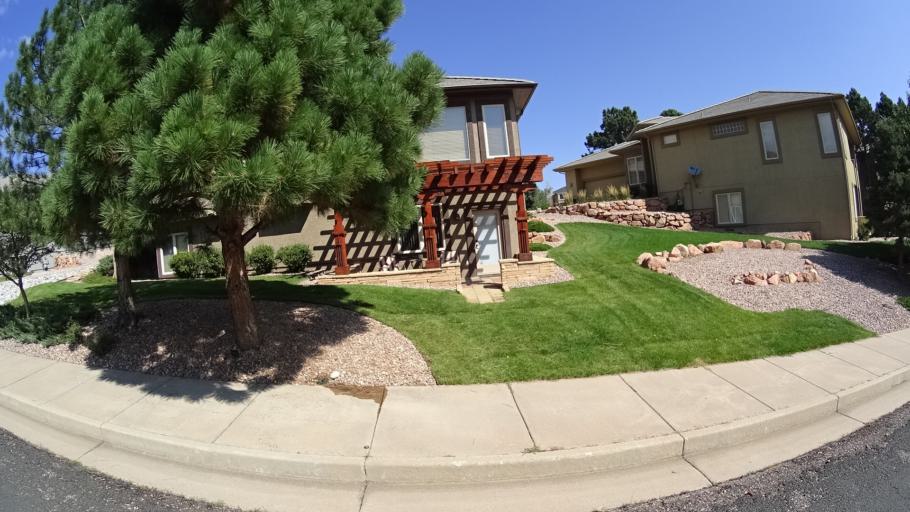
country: US
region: Colorado
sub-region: El Paso County
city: Manitou Springs
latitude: 38.9166
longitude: -104.8732
